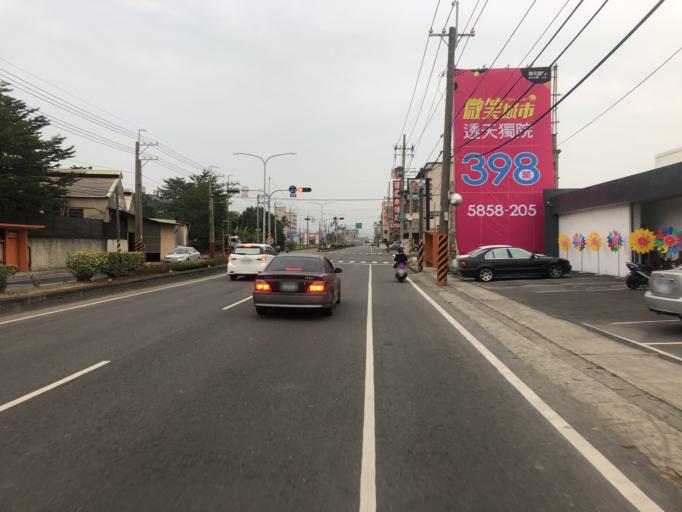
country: TW
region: Taiwan
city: Yujing
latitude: 23.1287
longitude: 120.3128
